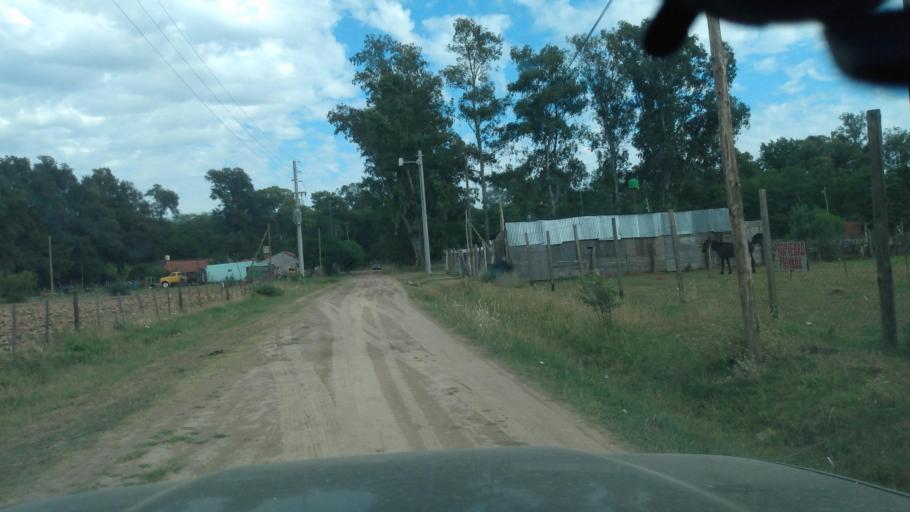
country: AR
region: Buenos Aires
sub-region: Partido de Lujan
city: Lujan
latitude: -34.5994
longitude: -59.0571
